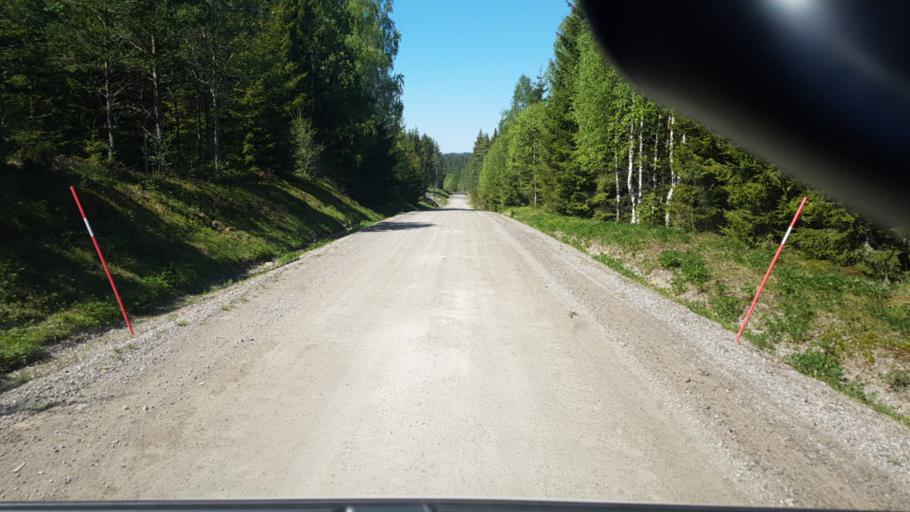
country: SE
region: Vaermland
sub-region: Arvika Kommun
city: Arvika
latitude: 59.8833
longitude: 12.6763
